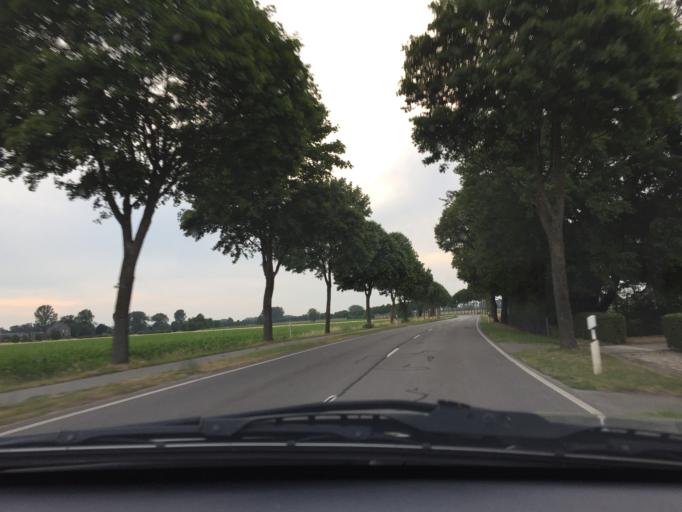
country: DE
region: North Rhine-Westphalia
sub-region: Regierungsbezirk Dusseldorf
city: Emmerich
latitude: 51.7821
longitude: 6.2238
